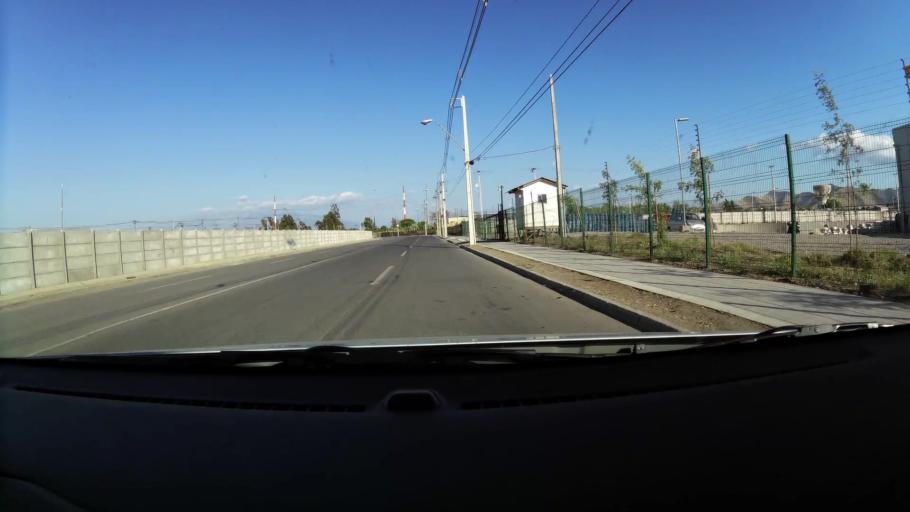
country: CL
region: Santiago Metropolitan
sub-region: Provincia de Maipo
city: San Bernardo
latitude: -33.5404
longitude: -70.7674
